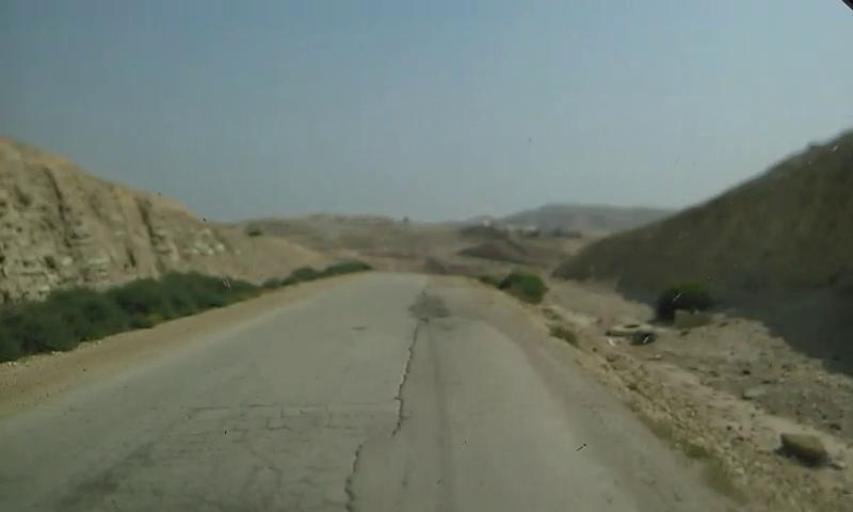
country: PS
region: West Bank
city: Jericho
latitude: 31.7915
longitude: 35.4279
